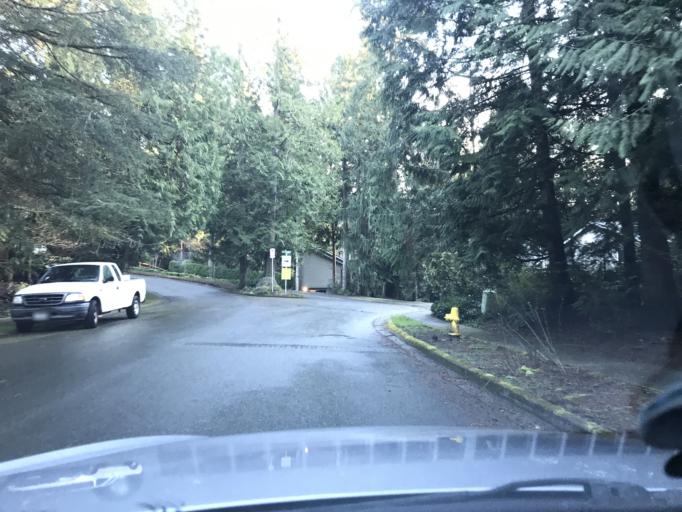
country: US
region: Washington
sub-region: King County
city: Sammamish
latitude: 47.6388
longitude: -122.1082
